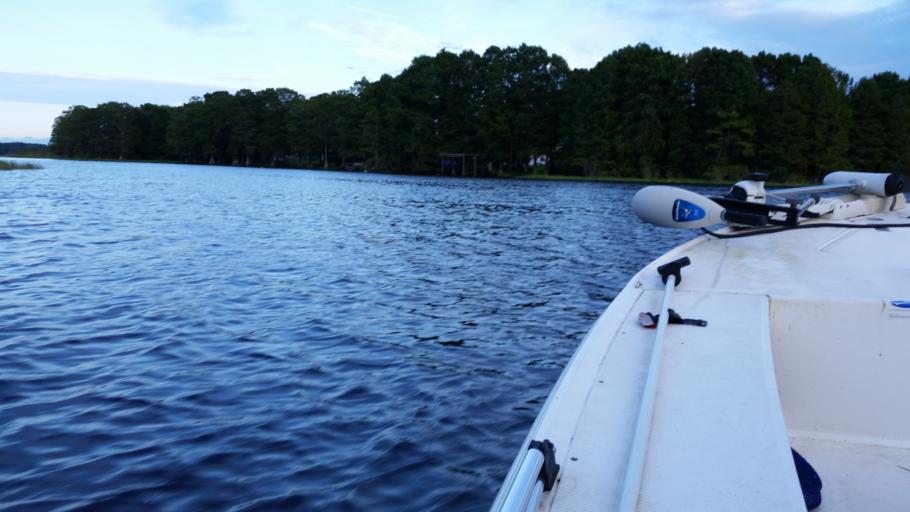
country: US
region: Florida
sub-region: Citrus County
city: Inverness
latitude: 28.8310
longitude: -82.3122
